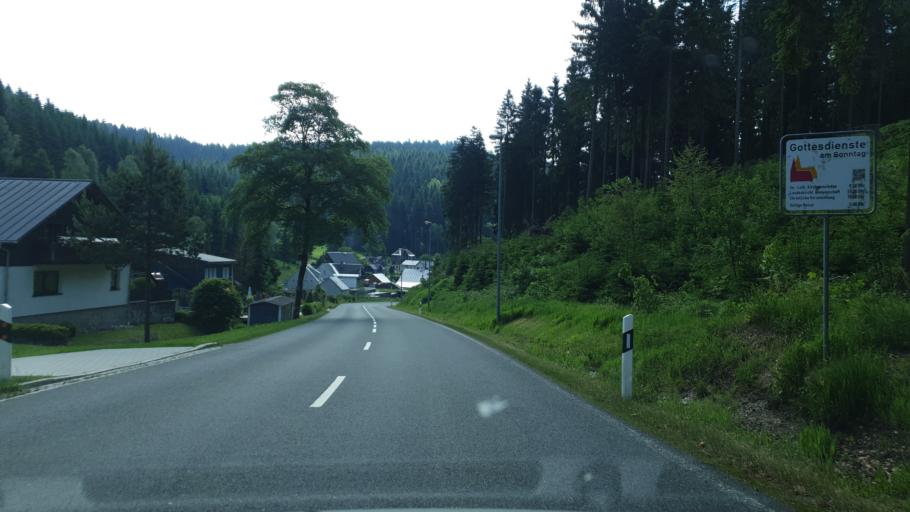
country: DE
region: Saxony
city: Klingenthal
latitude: 50.3991
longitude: 12.4935
